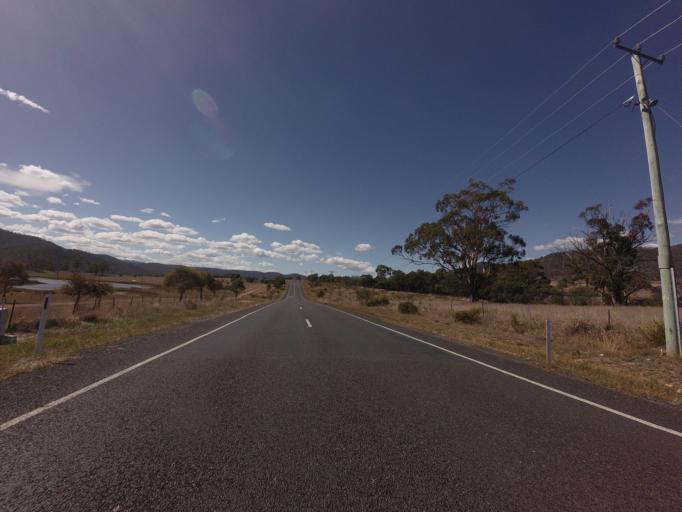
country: AU
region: Tasmania
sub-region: Break O'Day
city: St Helens
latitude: -41.7158
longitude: 147.8357
